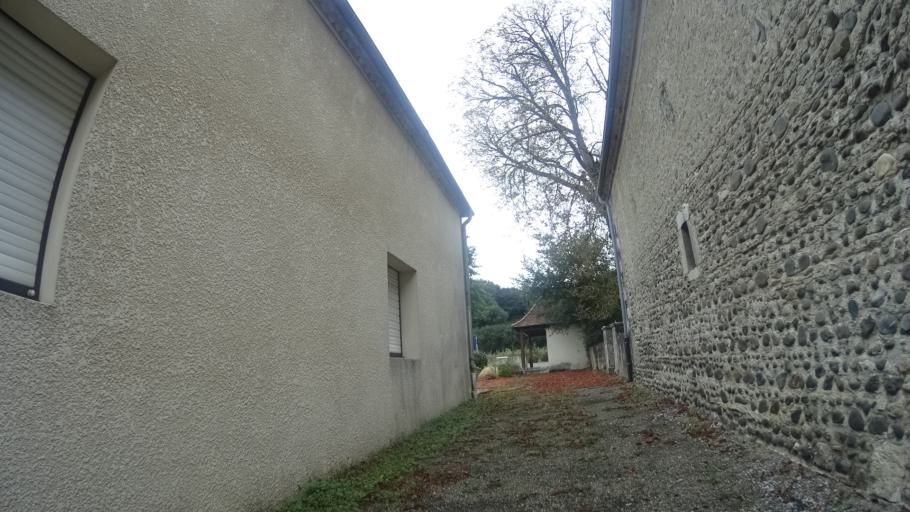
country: FR
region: Aquitaine
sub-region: Departement des Pyrenees-Atlantiques
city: Orthez
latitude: 43.4686
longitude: -0.7132
